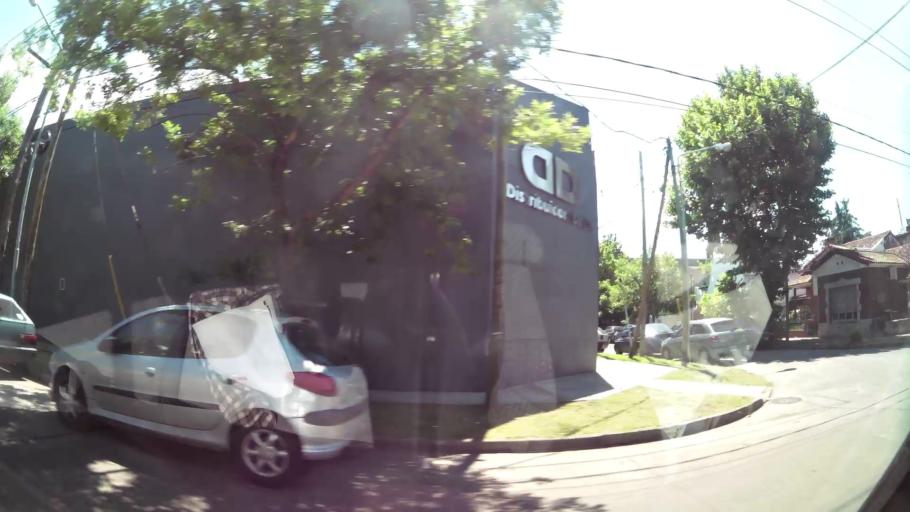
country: AR
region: Buenos Aires
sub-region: Partido de Tigre
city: Tigre
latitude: -34.4317
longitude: -58.5713
